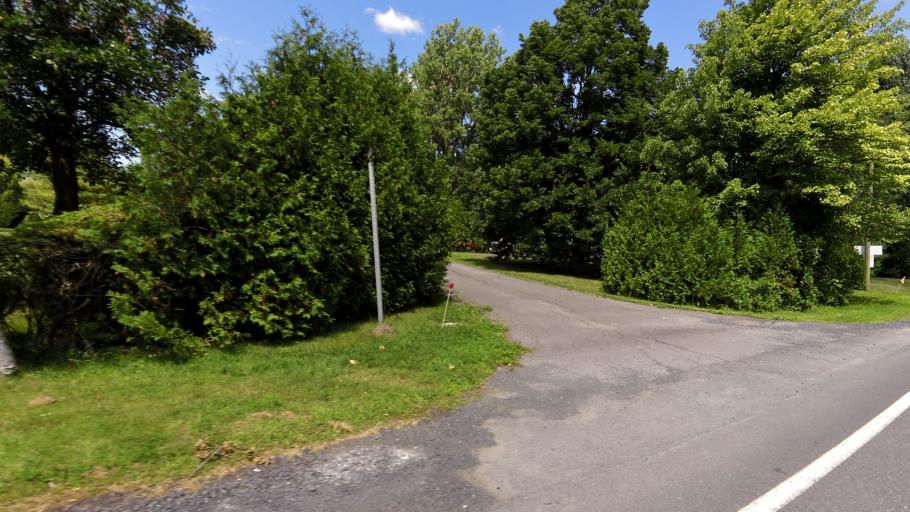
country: CA
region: Quebec
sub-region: Monteregie
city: Saint-Jean-sur-Richelieu
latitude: 45.3633
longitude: -73.2453
